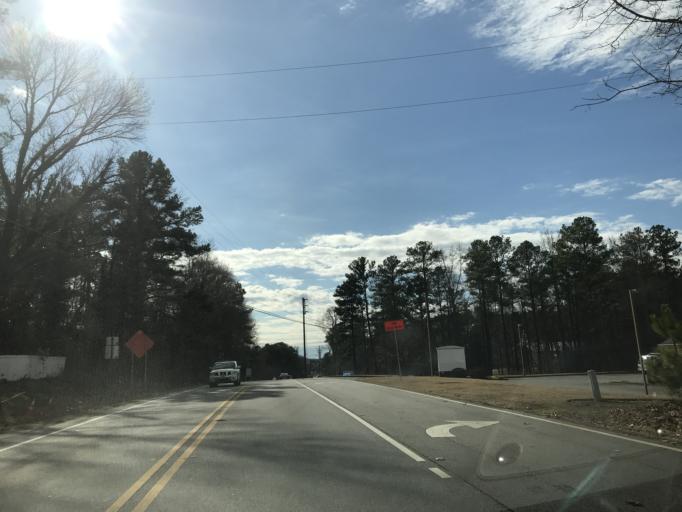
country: US
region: Georgia
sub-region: Paulding County
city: Hiram
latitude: 33.8888
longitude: -84.7561
